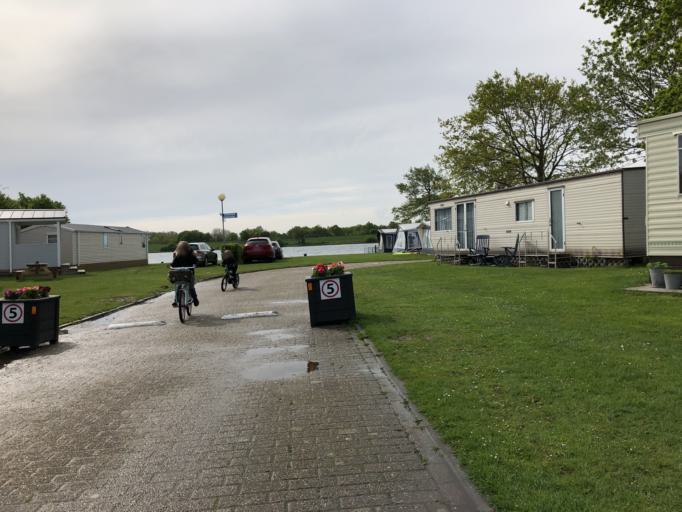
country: NL
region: Zeeland
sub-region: Gemeente Goes
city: Goes
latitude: 51.5485
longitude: 3.8053
